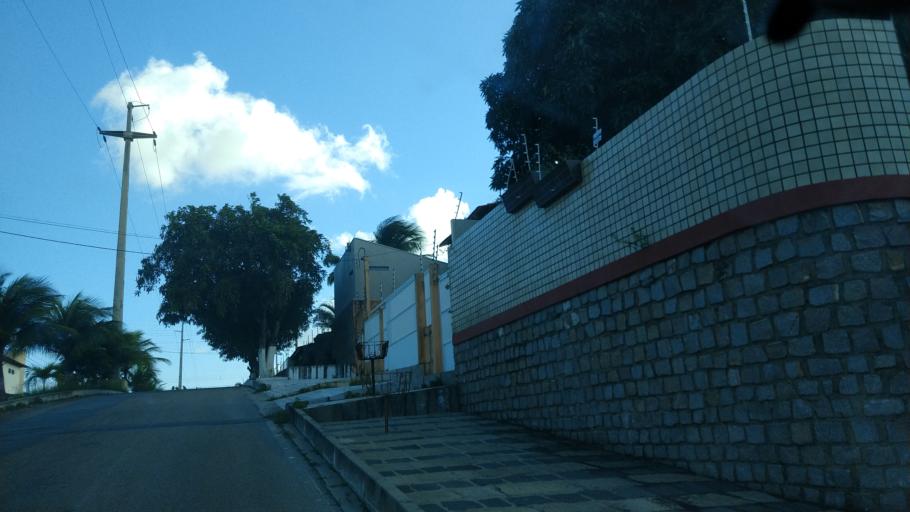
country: BR
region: Rio Grande do Norte
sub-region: Natal
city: Natal
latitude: -5.8470
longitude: -35.2041
